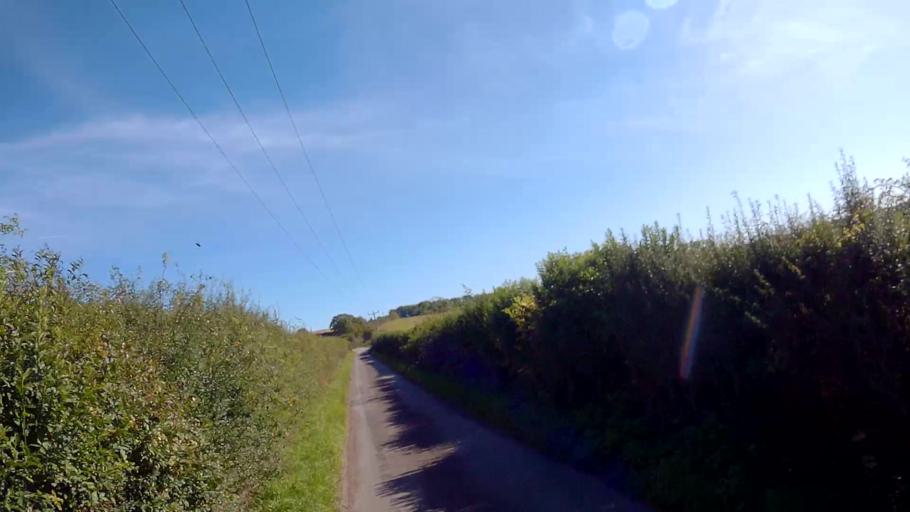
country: GB
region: England
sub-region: Hampshire
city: Andover
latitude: 51.1622
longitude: -1.4047
